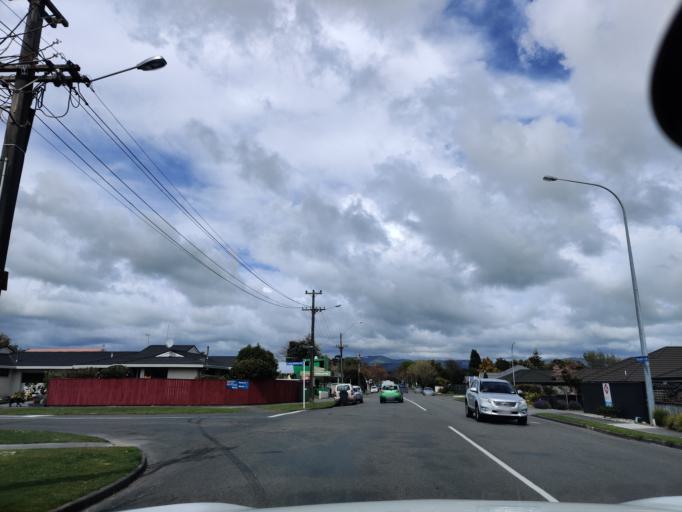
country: NZ
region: Manawatu-Wanganui
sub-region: Palmerston North City
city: Palmerston North
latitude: -40.3791
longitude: 175.5845
